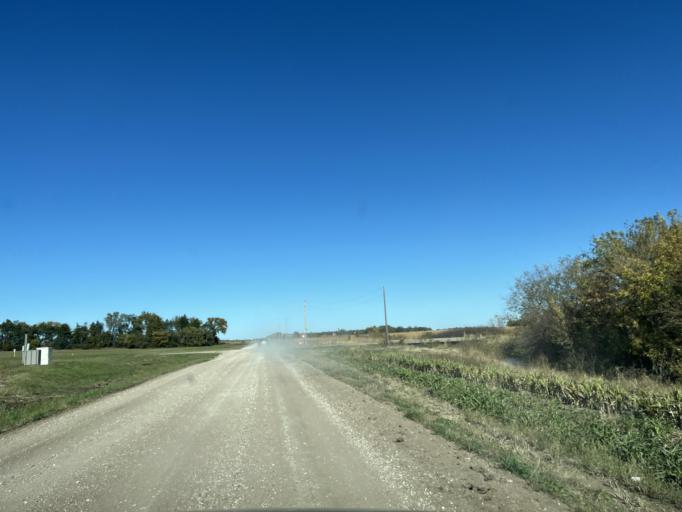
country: US
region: Kansas
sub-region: McPherson County
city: Moundridge
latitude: 38.2170
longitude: -97.6292
